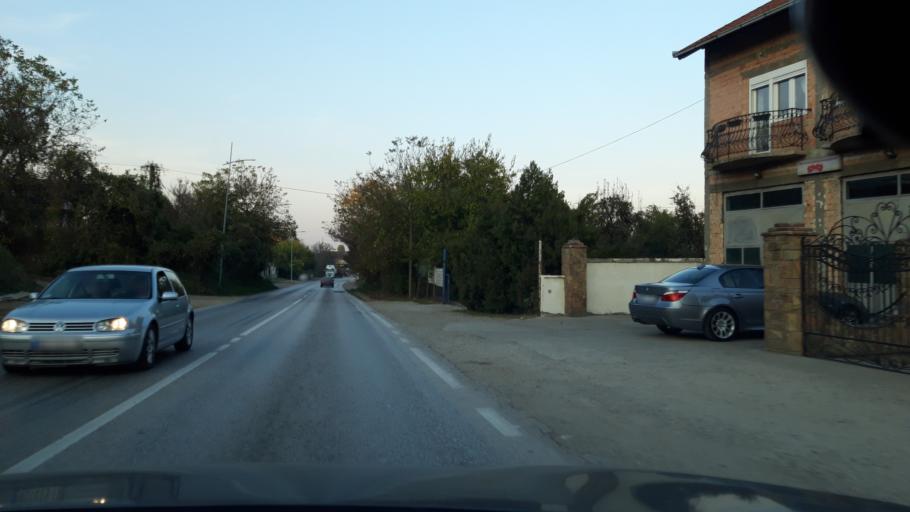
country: RS
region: Autonomna Pokrajina Vojvodina
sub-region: Juznobacki Okrug
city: Petrovaradin
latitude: 45.2266
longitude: 19.8793
